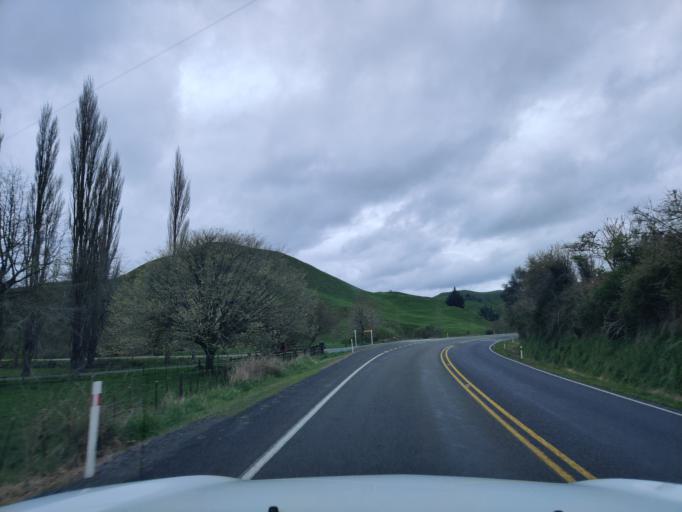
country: NZ
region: Waikato
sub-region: Otorohanga District
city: Otorohanga
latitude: -38.5244
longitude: 175.1754
